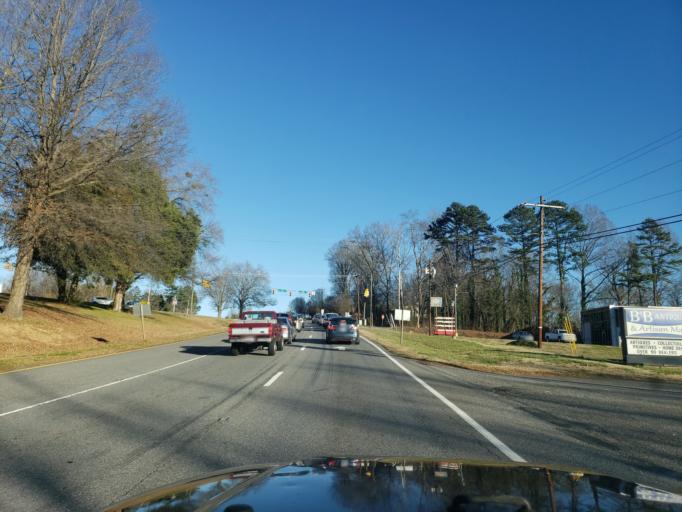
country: US
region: North Carolina
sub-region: Gaston County
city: Bessemer City
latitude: 35.2566
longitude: -81.2418
